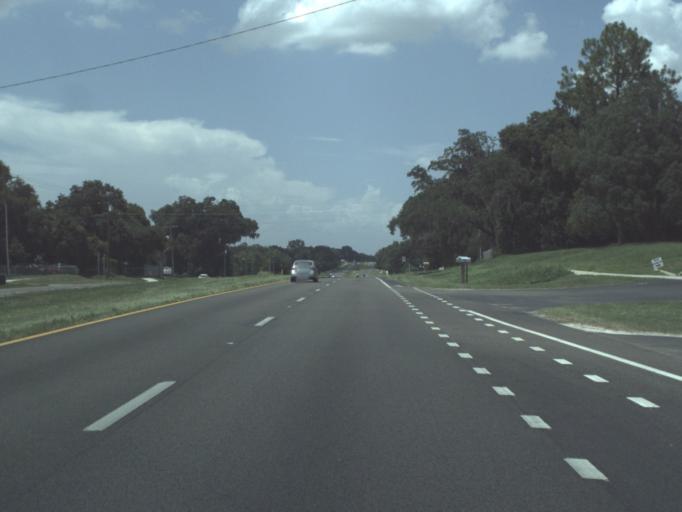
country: US
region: Florida
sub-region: Pasco County
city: Dade City North
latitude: 28.4239
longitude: -82.1906
